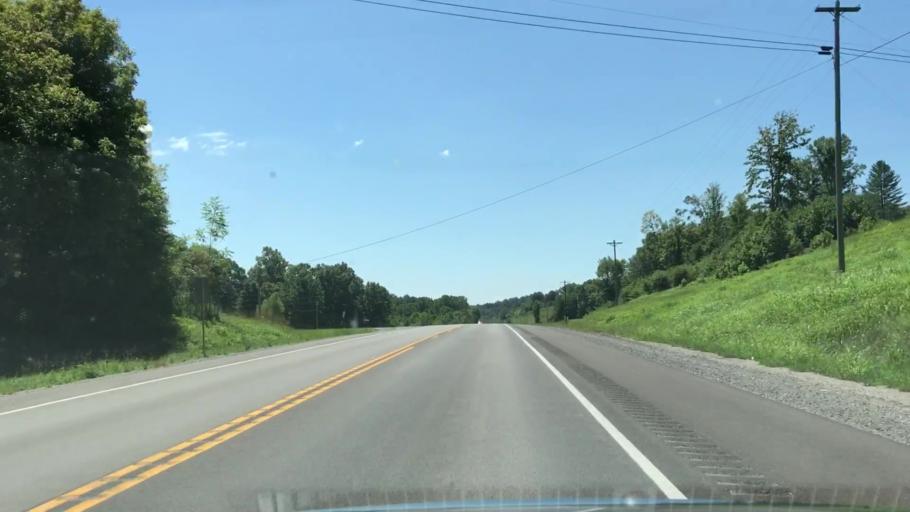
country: US
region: Kentucky
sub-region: Cumberland County
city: Burkesville
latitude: 36.7011
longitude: -85.3722
